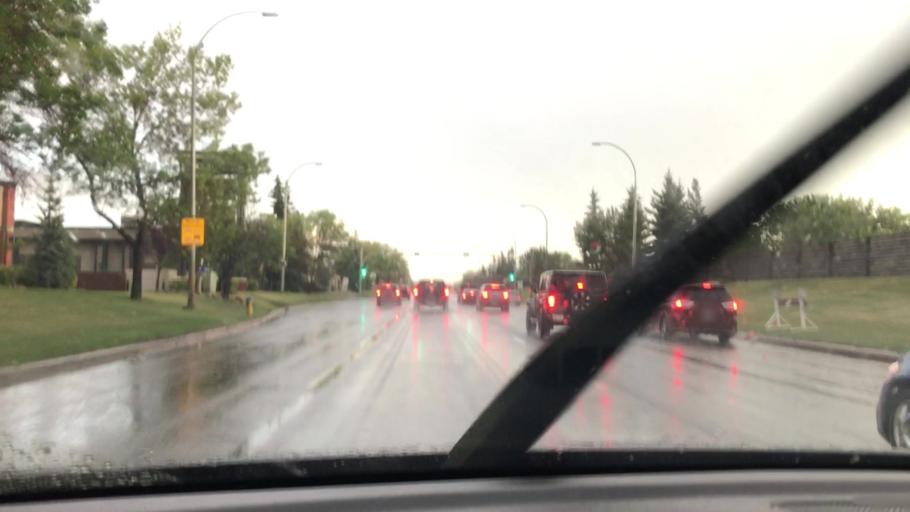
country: CA
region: Alberta
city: Edmonton
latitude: 53.4732
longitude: -113.4957
